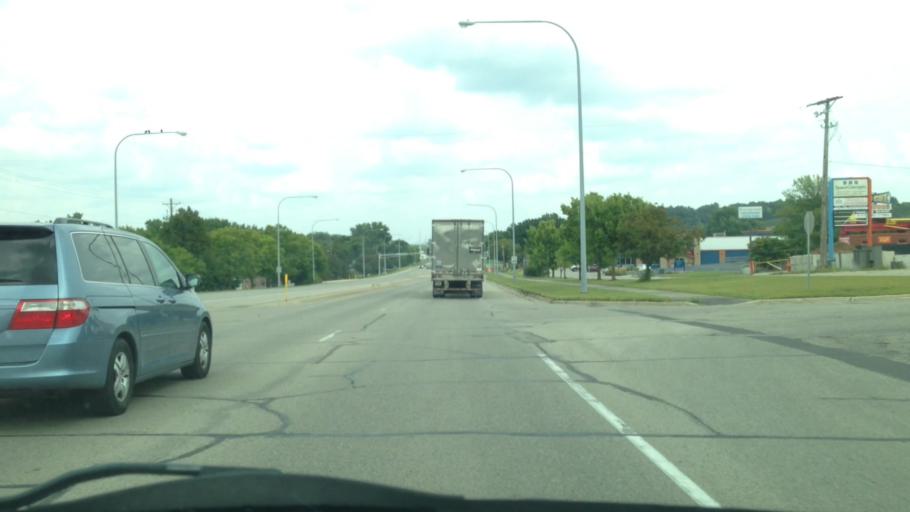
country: US
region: Minnesota
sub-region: Olmsted County
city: Rochester
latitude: 44.0519
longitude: -92.4552
